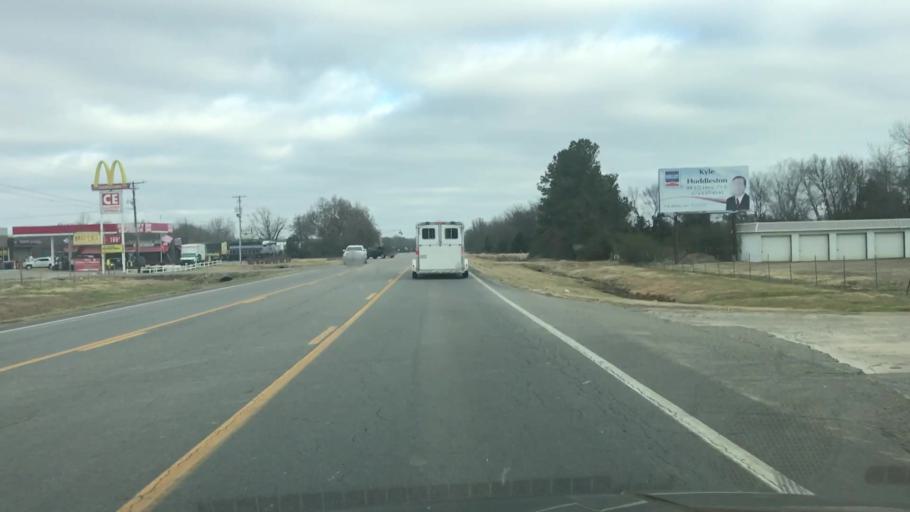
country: US
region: Arkansas
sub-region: Scott County
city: Waldron
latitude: 34.9033
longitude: -94.1074
